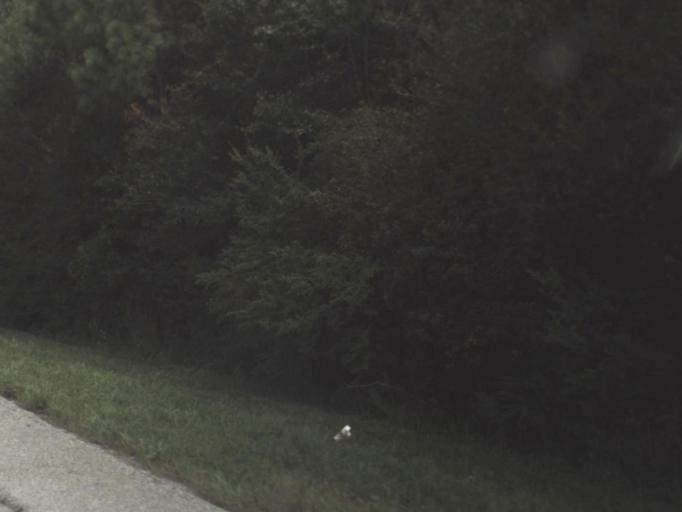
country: US
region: Florida
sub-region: Hardee County
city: Zolfo Springs
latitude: 27.3816
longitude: -81.7948
